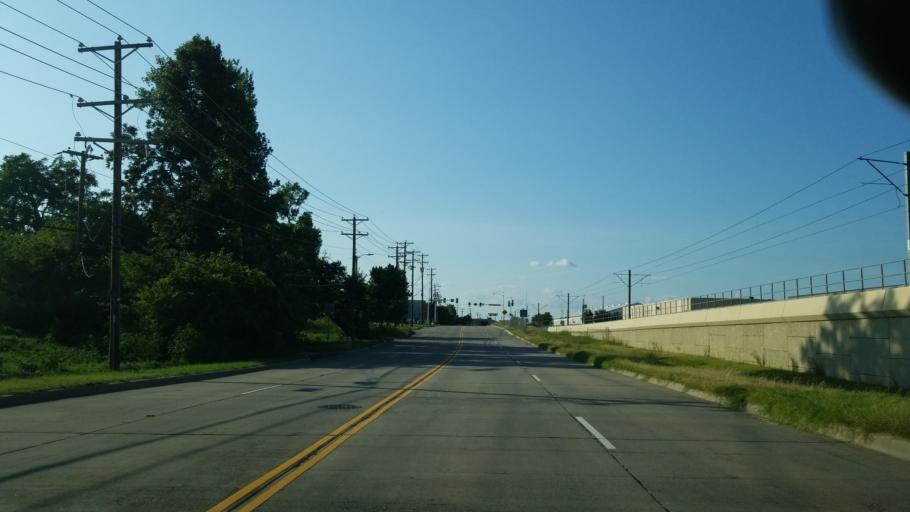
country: US
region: Texas
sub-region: Dallas County
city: Farmers Branch
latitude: 32.9324
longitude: -96.8997
